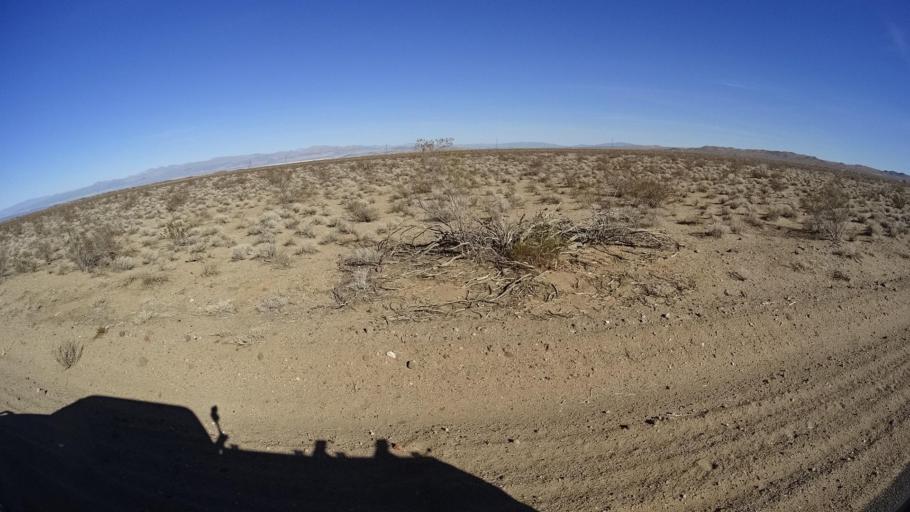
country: US
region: California
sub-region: Kern County
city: China Lake Acres
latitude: 35.5796
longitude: -117.7865
